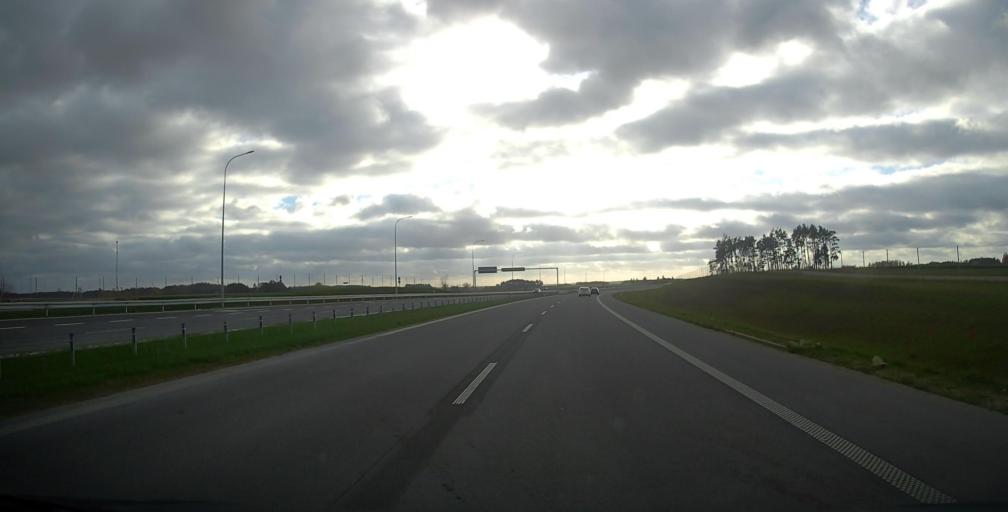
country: PL
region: Podlasie
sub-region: Powiat grajewski
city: Szczuczyn
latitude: 53.5865
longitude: 22.3271
